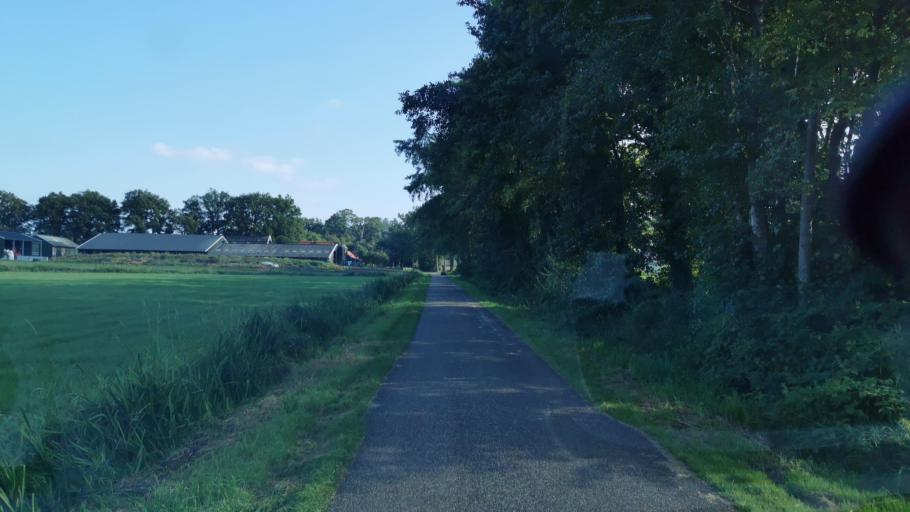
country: NL
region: Overijssel
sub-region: Gemeente Tubbergen
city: Tubbergen
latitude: 52.3529
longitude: 6.8155
